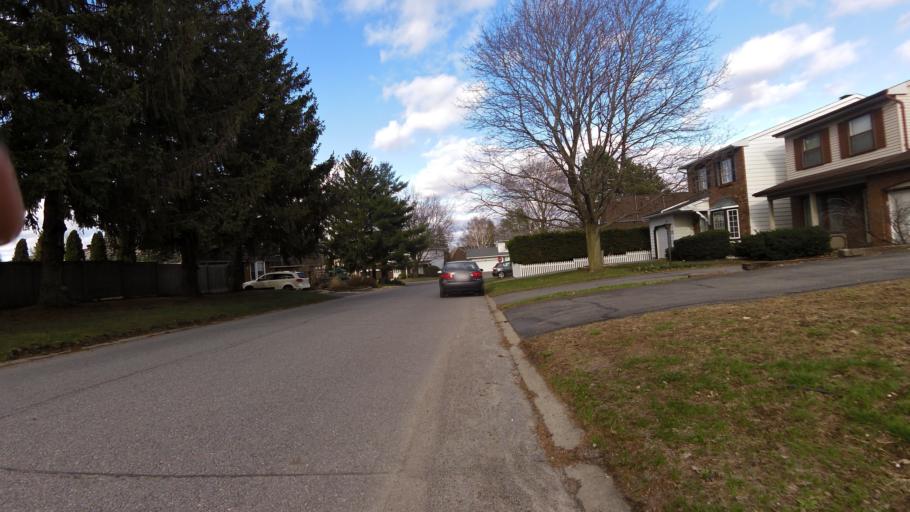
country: CA
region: Ontario
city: Bells Corners
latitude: 45.3294
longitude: -75.7732
